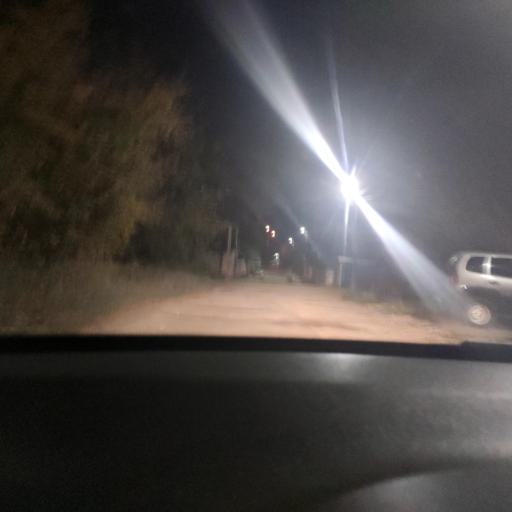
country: RU
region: Samara
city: Samara
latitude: 53.2244
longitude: 50.2184
